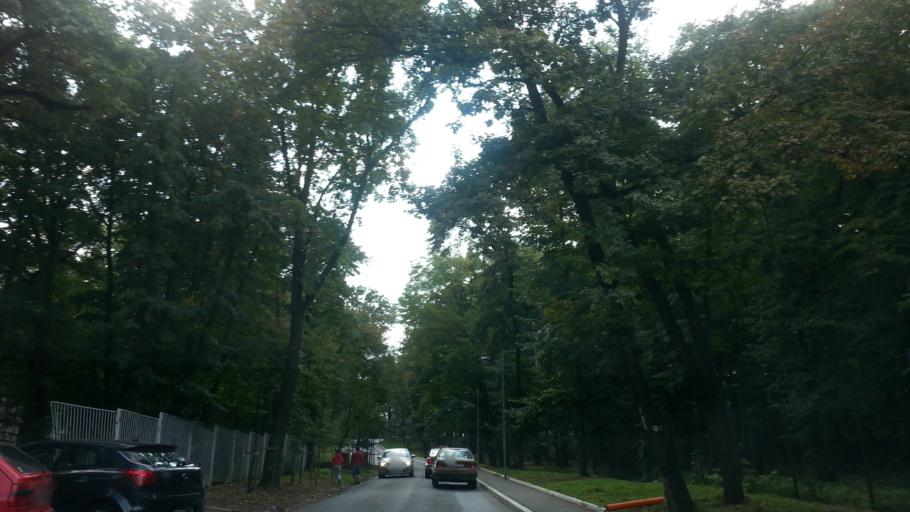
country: RS
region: Central Serbia
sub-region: Belgrade
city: Rakovica
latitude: 44.7614
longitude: 20.4348
